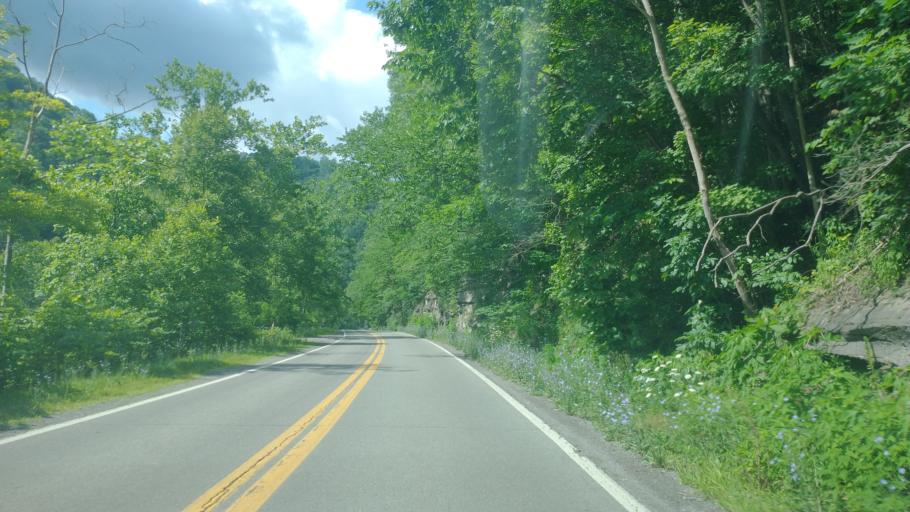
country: US
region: West Virginia
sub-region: McDowell County
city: Welch
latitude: 37.4129
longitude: -81.5286
